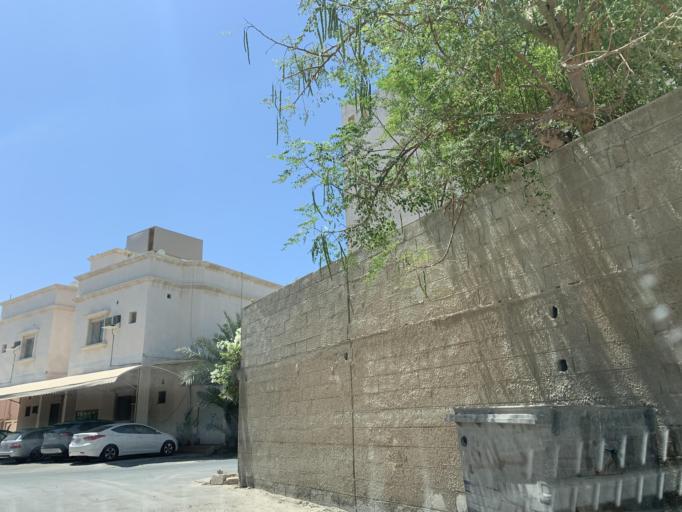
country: BH
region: Manama
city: Jidd Hafs
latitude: 26.2323
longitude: 50.4879
